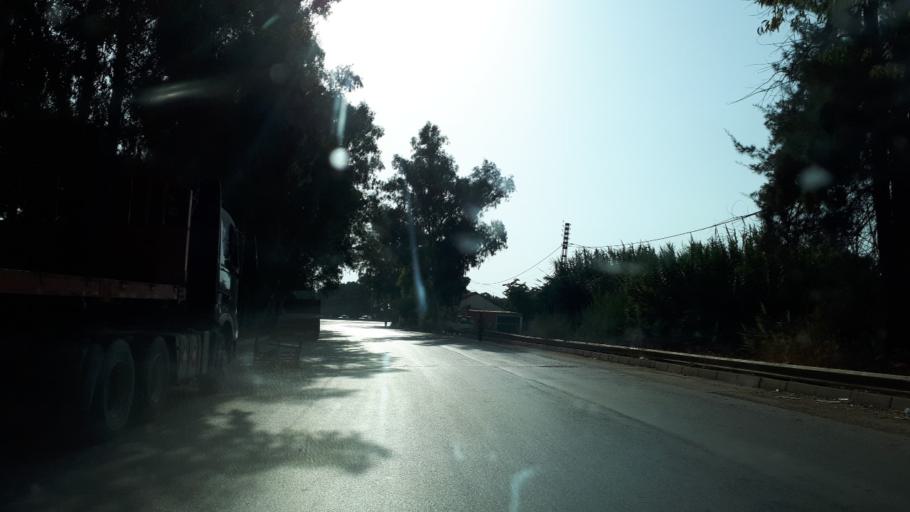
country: DZ
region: Alger
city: Dar el Beida
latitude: 36.7279
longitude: 3.2130
